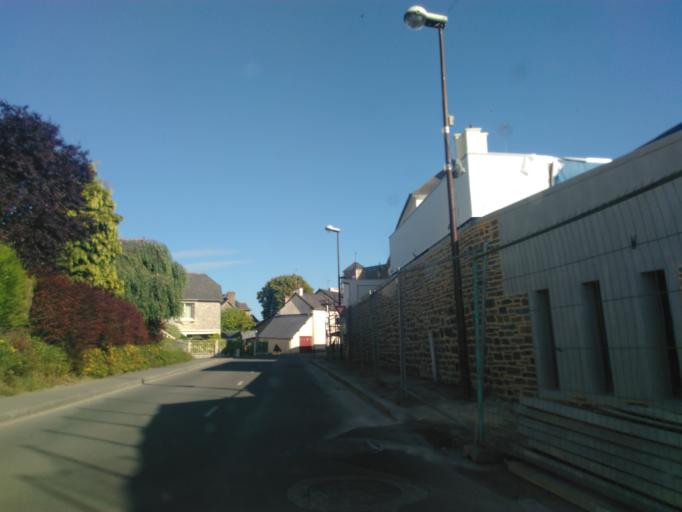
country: FR
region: Brittany
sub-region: Departement d'Ille-et-Vilaine
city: La Meziere
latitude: 48.2205
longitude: -1.7571
